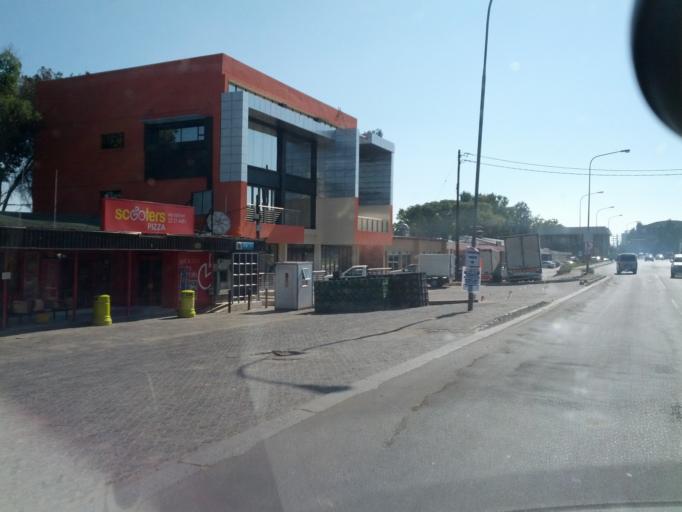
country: LS
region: Maseru
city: Maseru
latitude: -29.2994
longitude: 27.4706
